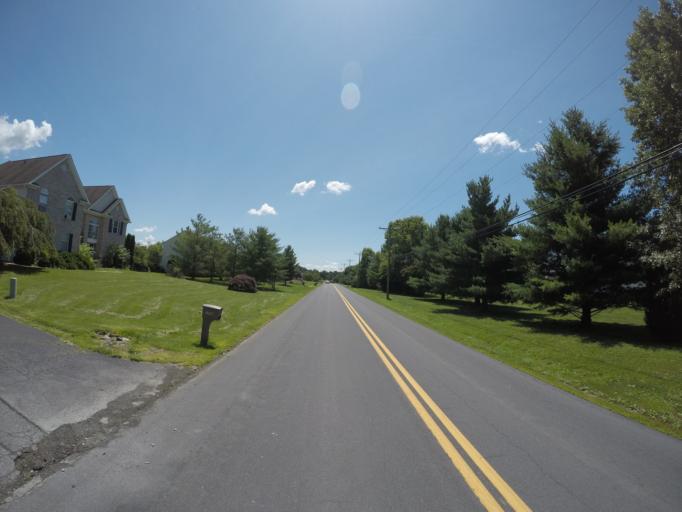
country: US
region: Delaware
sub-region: New Castle County
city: Glasgow
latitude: 39.5669
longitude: -75.6915
